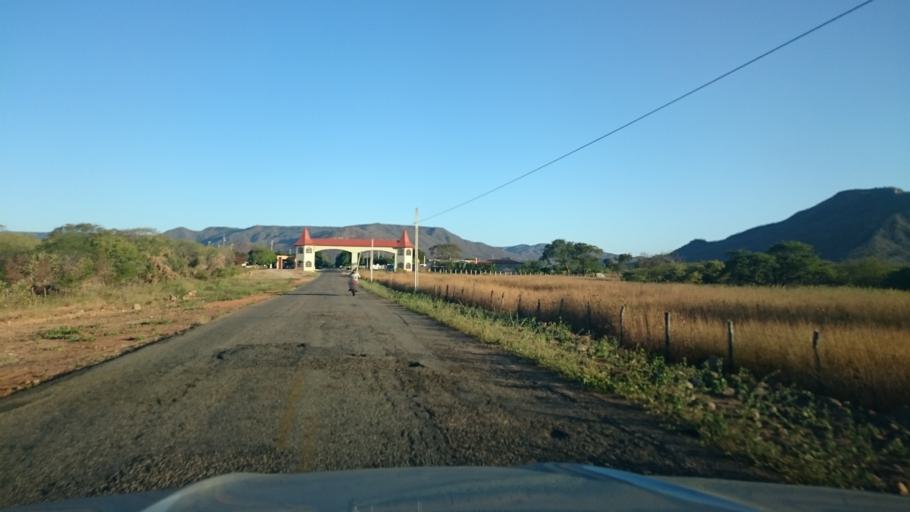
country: BR
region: Rio Grande do Norte
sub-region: Umarizal
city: Umarizal
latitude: -5.9870
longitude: -37.9490
